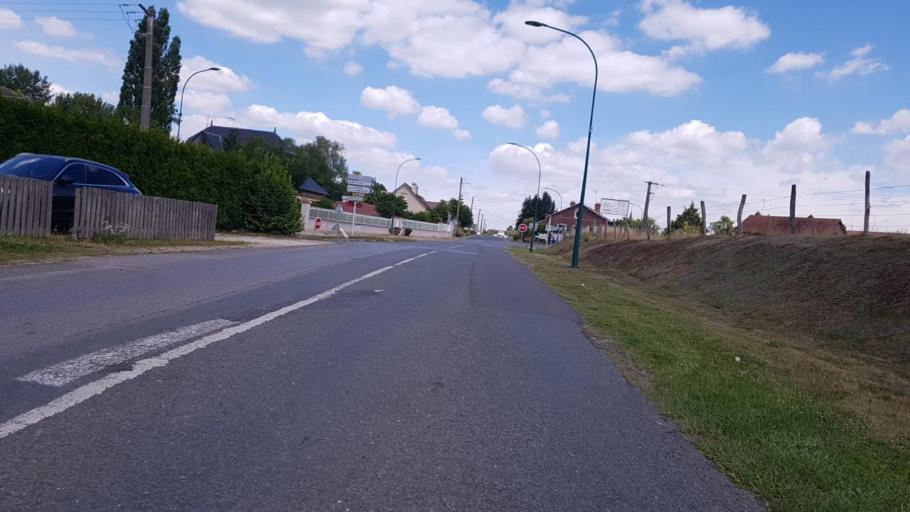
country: FR
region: Picardie
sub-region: Departement de l'Oise
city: Tracy-le-Mont
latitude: 49.4946
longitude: 2.9678
